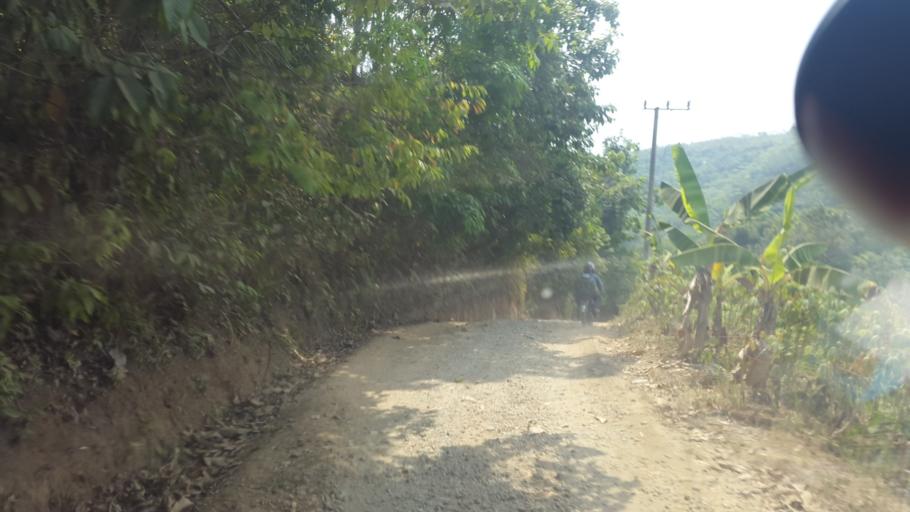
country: ID
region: West Java
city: Sindangsari
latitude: -6.9605
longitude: 106.6874
